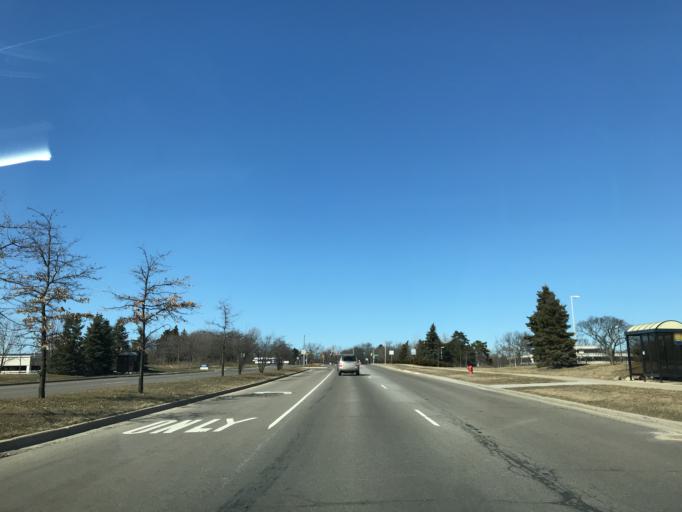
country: US
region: Michigan
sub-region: Washtenaw County
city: Ann Arbor
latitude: 42.3000
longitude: -83.7042
